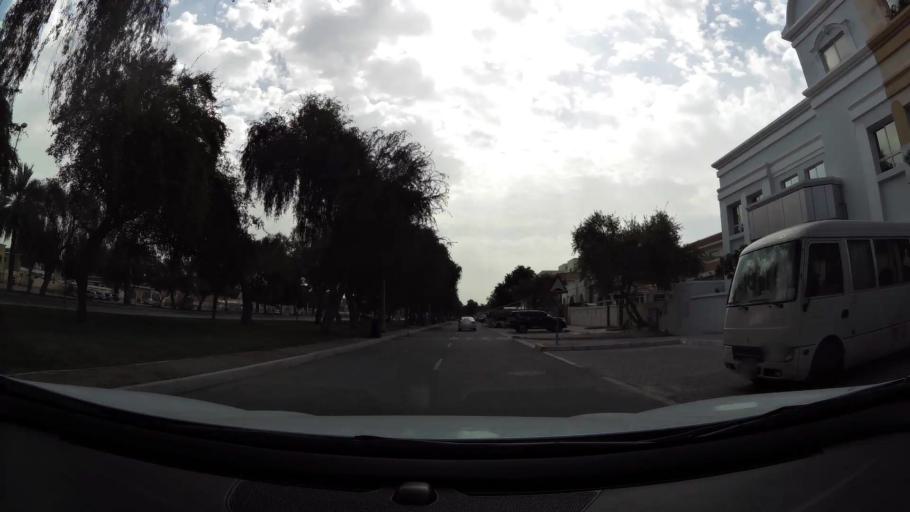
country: AE
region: Abu Dhabi
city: Abu Dhabi
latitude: 24.4421
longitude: 54.3688
